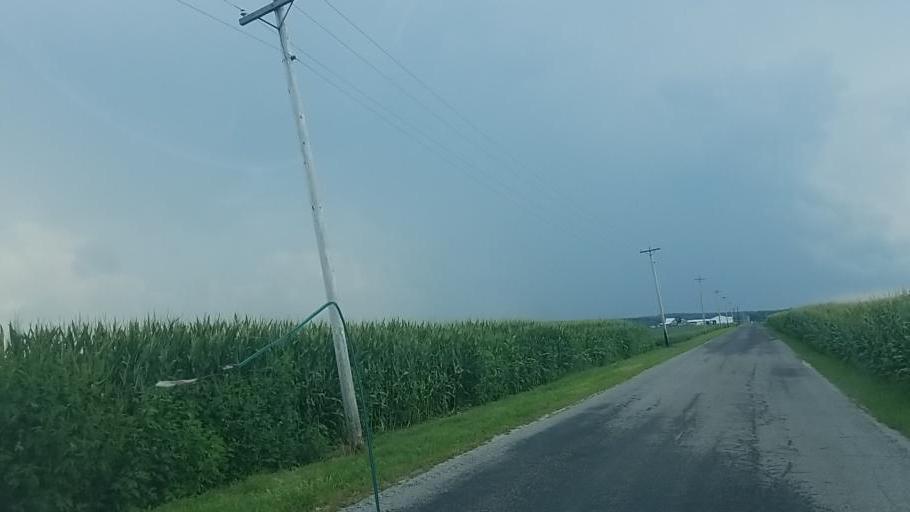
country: US
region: Ohio
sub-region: Medina County
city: Lodi
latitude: 41.0162
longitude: -82.0183
